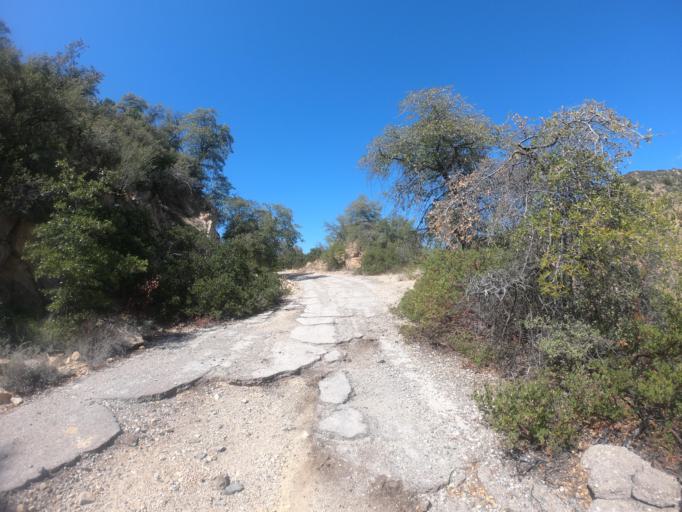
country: US
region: Arizona
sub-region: Gila County
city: Miami
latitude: 33.3584
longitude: -110.9498
